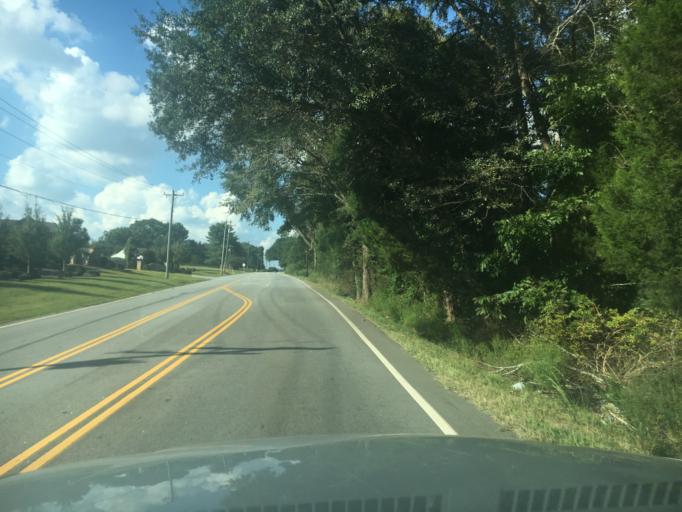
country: US
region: South Carolina
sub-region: Greenville County
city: Simpsonville
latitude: 34.6876
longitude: -82.2521
